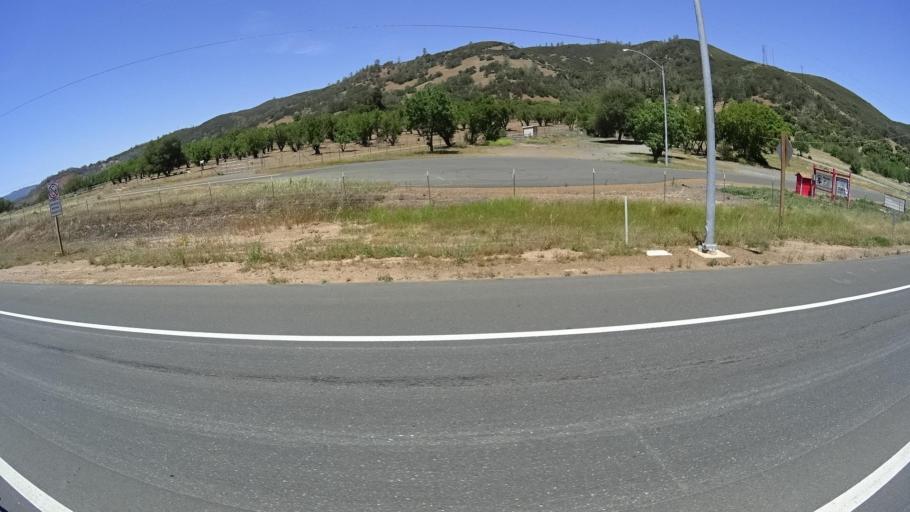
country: US
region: California
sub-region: Lake County
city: Clearlake
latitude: 39.0086
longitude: -122.6156
